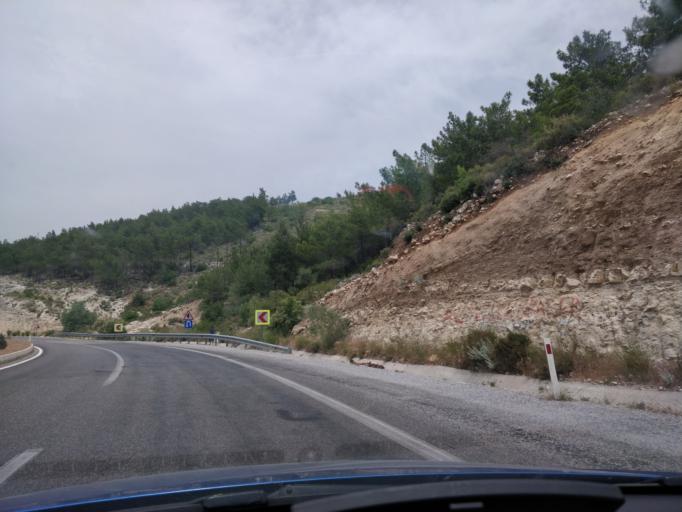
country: TR
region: Mersin
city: Tasucu
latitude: 36.3958
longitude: 33.8446
